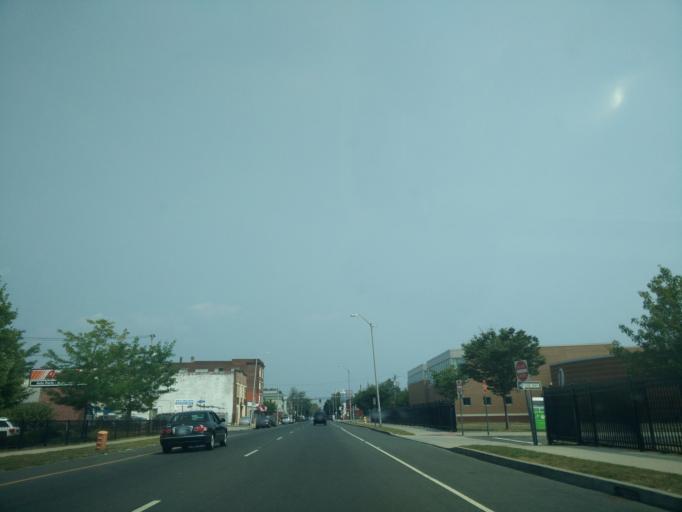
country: US
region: Connecticut
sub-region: Fairfield County
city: Bridgeport
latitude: 41.1706
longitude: -73.2084
